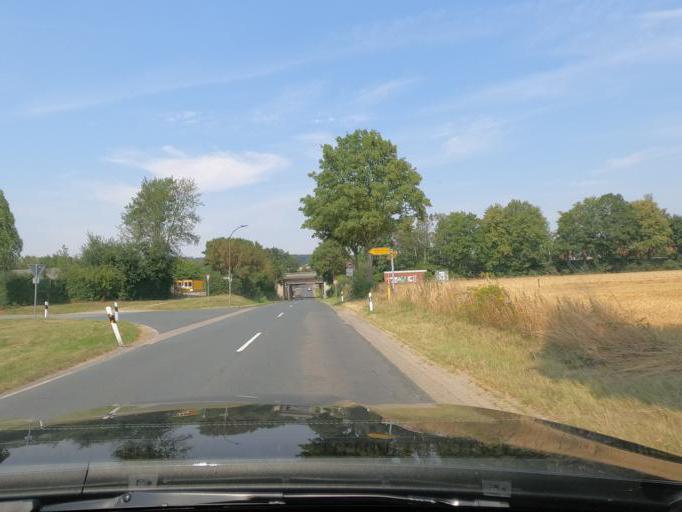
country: DE
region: Lower Saxony
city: Springe
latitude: 52.2105
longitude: 9.6291
